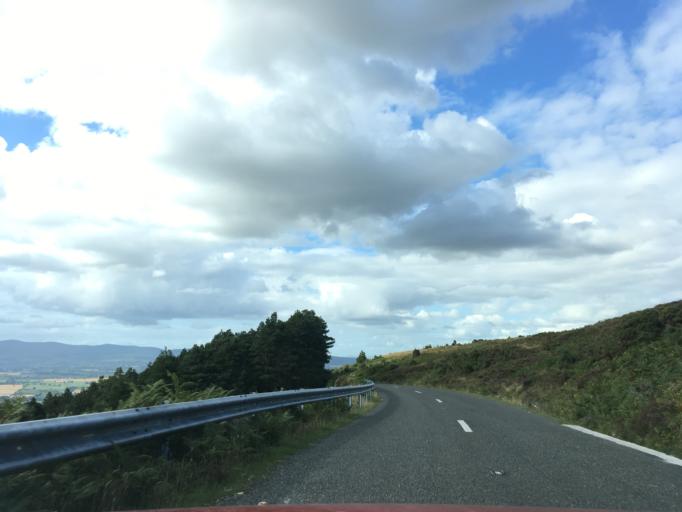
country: IE
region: Munster
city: Cahir
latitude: 52.2518
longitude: -7.9550
